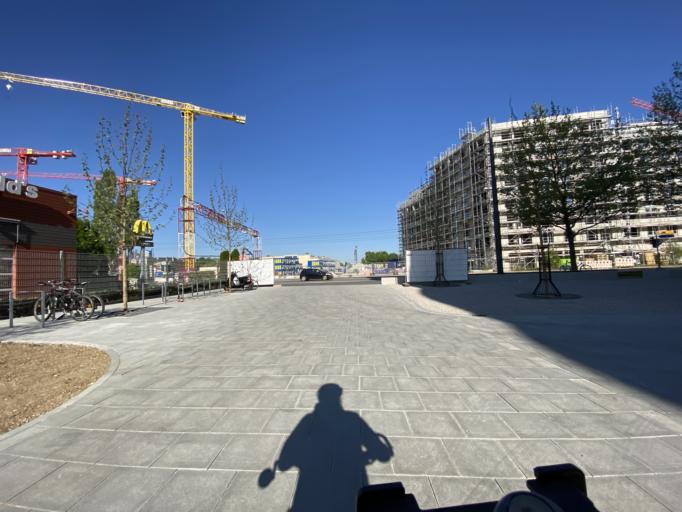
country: DE
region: Bavaria
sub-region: Upper Bavaria
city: Munich
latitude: 48.1212
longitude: 11.5860
